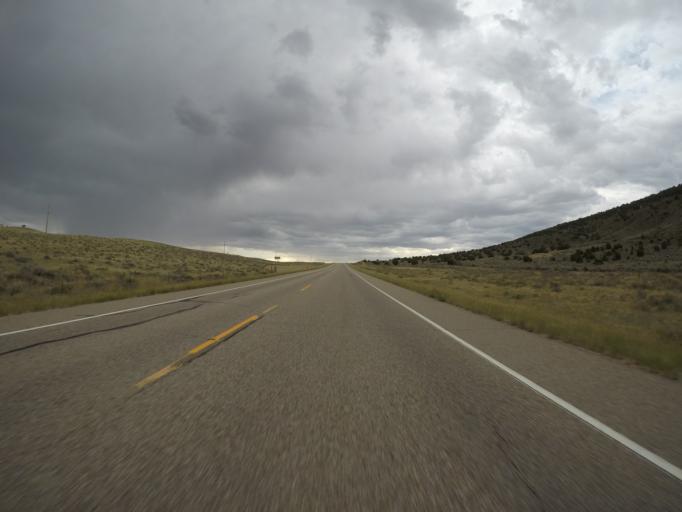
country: US
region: Colorado
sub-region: Rio Blanco County
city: Rangely
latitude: 40.3567
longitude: -108.4435
